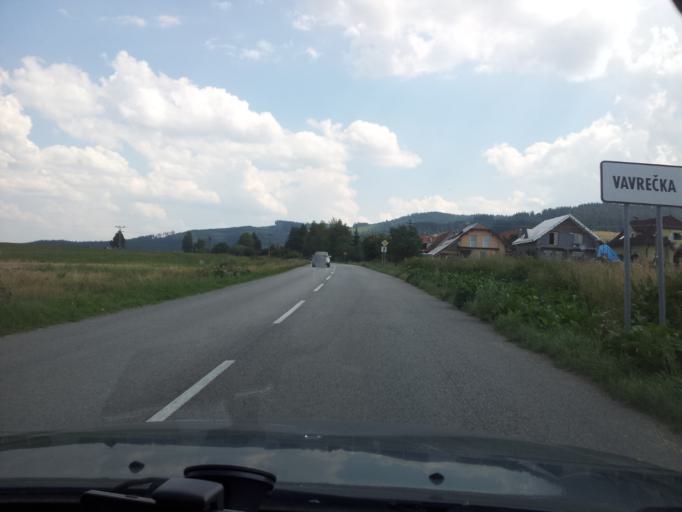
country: SK
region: Zilinsky
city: Namestovo
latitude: 49.3889
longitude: 19.4618
